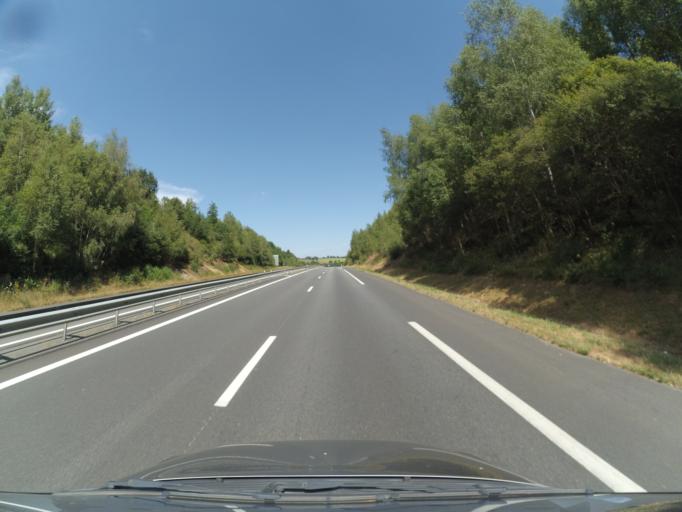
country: FR
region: Poitou-Charentes
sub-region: Departement de la Charente
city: Etagnac
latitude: 45.8956
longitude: 0.8270
